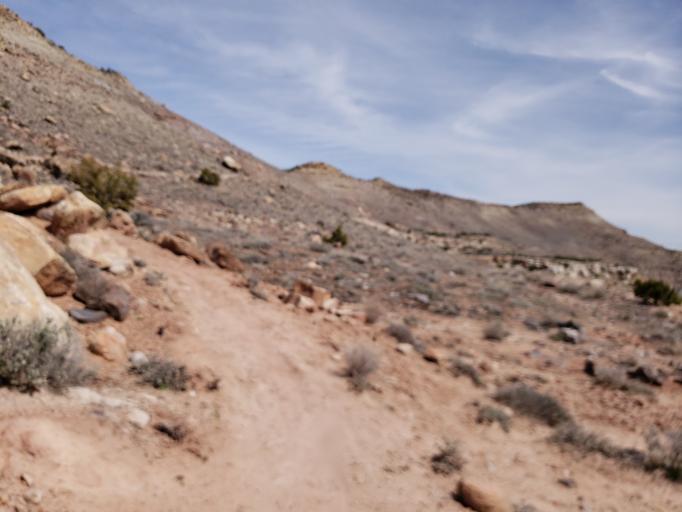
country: US
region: Colorado
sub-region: Mesa County
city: Loma
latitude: 39.1827
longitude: -108.8654
